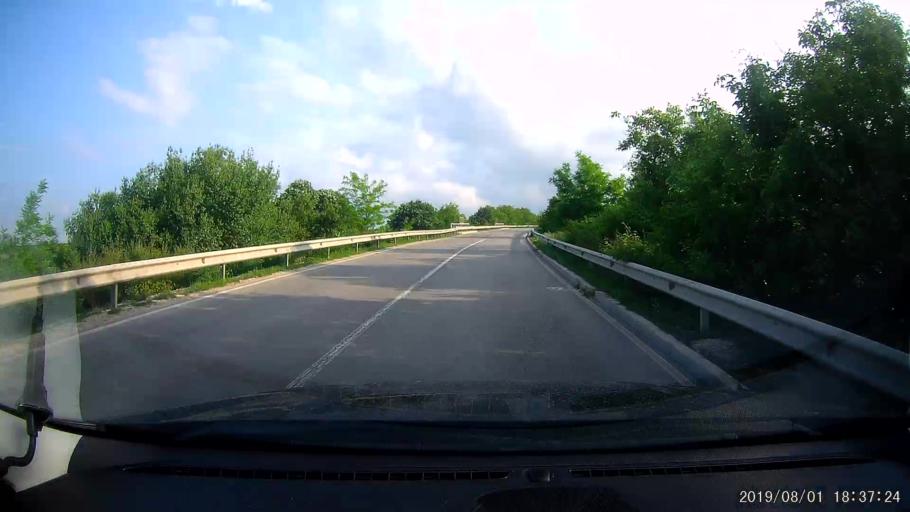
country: BG
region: Shumen
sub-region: Obshtina Khitrino
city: Gara Khitrino
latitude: 43.4218
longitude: 26.9306
